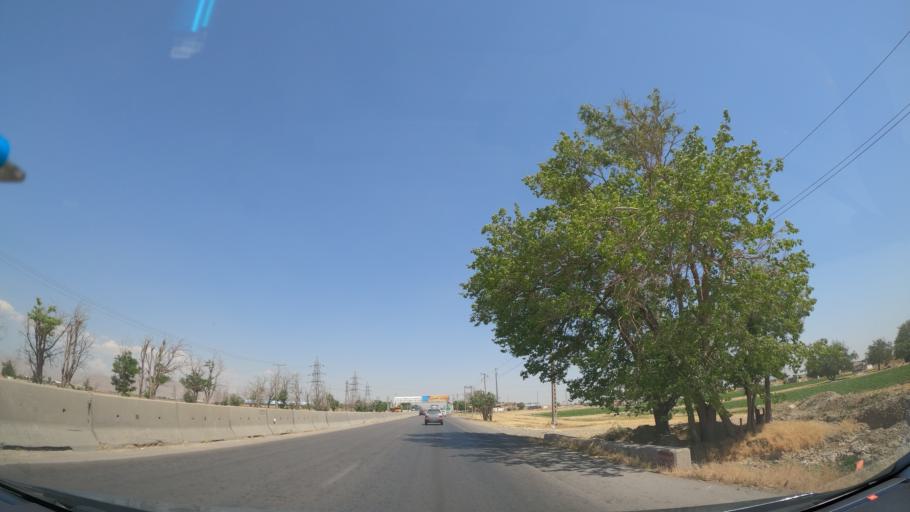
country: IR
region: Alborz
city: Hashtgerd
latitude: 35.9246
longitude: 50.7394
